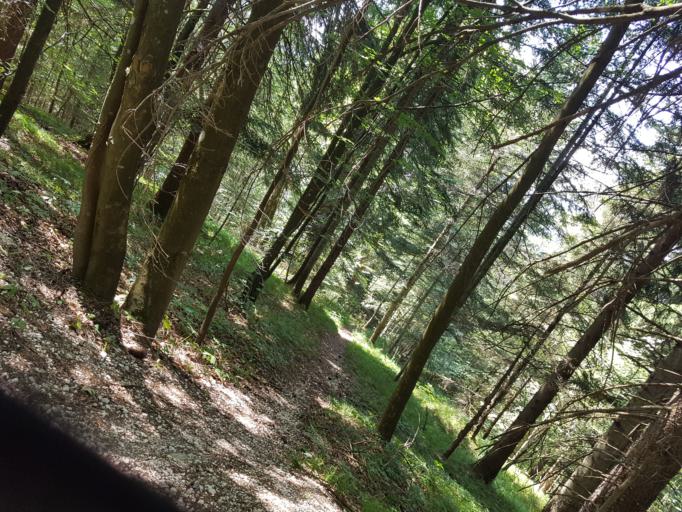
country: DE
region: Bavaria
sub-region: Upper Bavaria
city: Berchtesgaden
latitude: 47.6530
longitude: 13.0187
